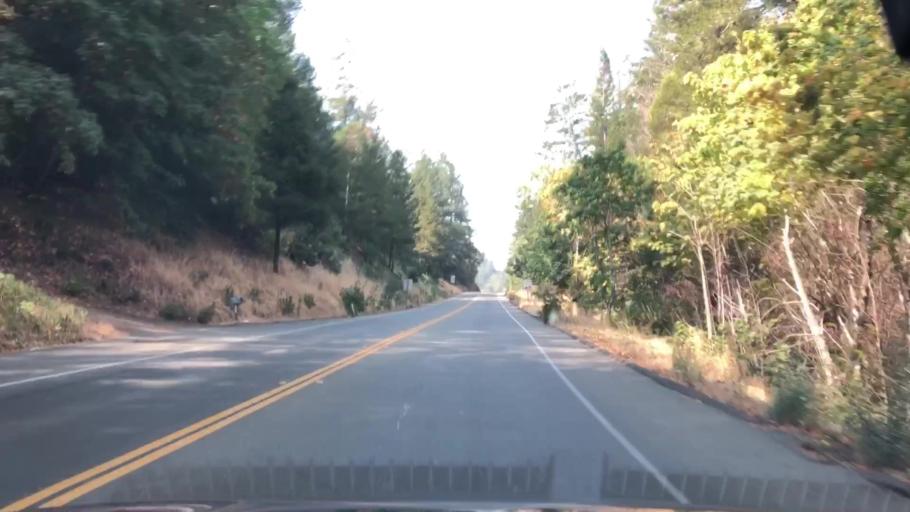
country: US
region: California
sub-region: Napa County
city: Calistoga
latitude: 38.5775
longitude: -122.6202
